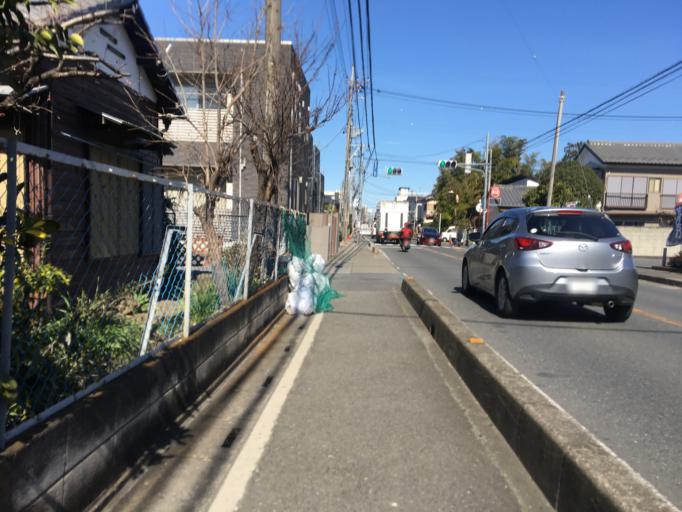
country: JP
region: Saitama
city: Shiki
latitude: 35.8121
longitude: 139.5668
